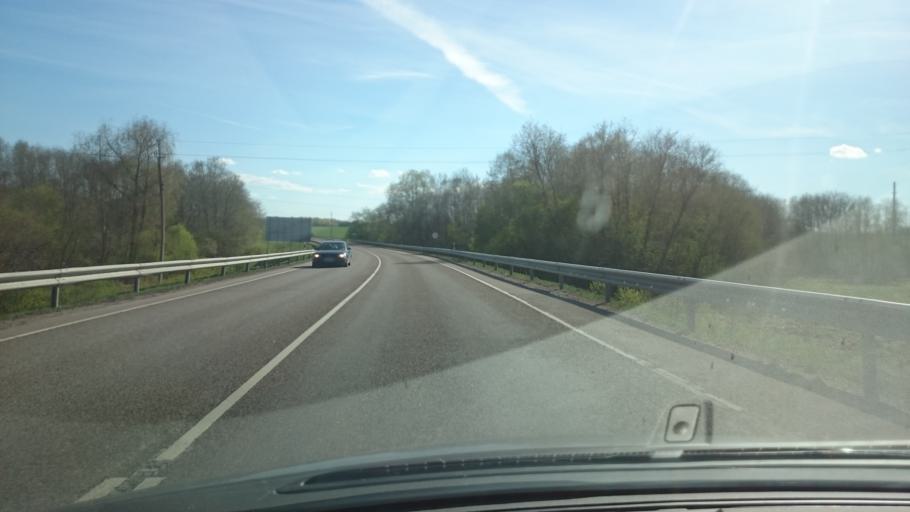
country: EE
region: Laeaene-Virumaa
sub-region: Kadrina vald
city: Kadrina
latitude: 59.3446
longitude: 26.1235
